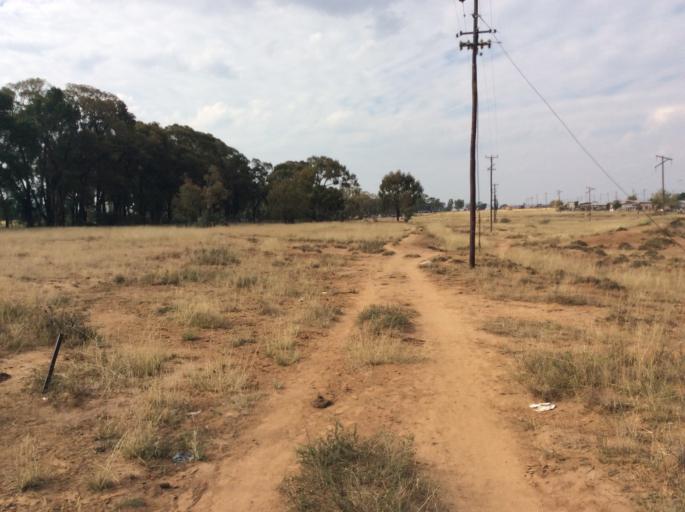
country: ZA
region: Orange Free State
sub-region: Xhariep District Municipality
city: Dewetsdorp
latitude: -29.5781
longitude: 26.6771
